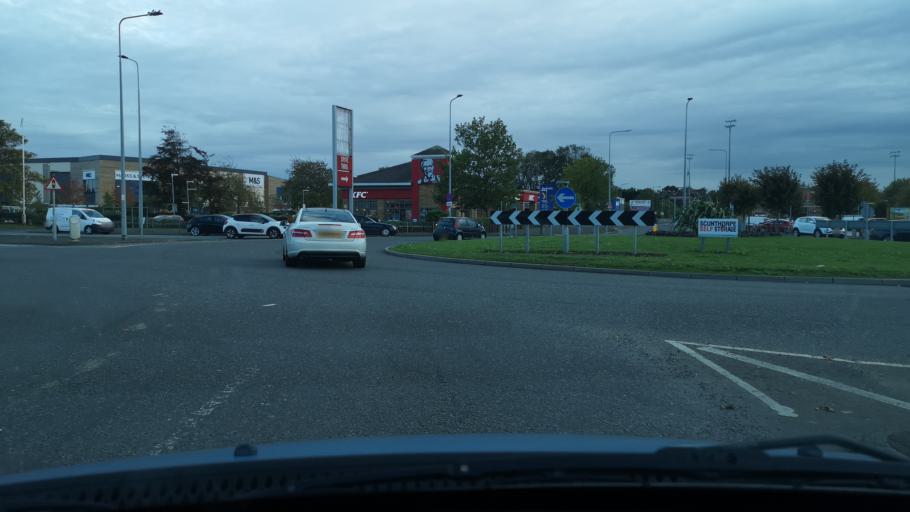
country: GB
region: England
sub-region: North Lincolnshire
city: Gunness
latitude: 53.5896
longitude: -0.6943
